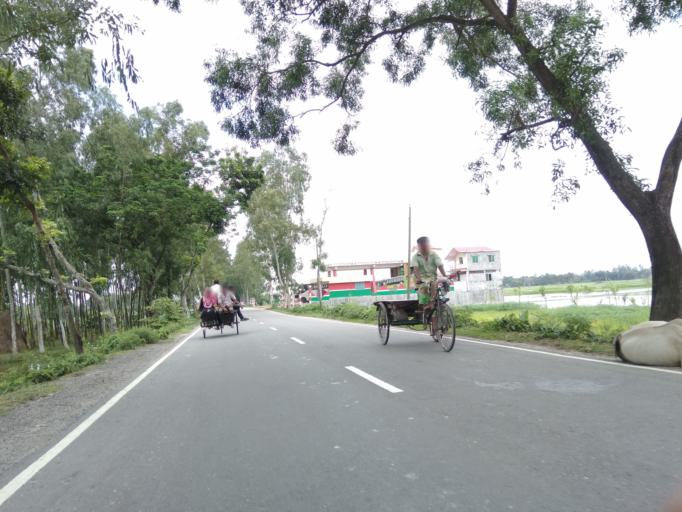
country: BD
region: Rajshahi
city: Saidpur
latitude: 25.7688
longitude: 88.8136
